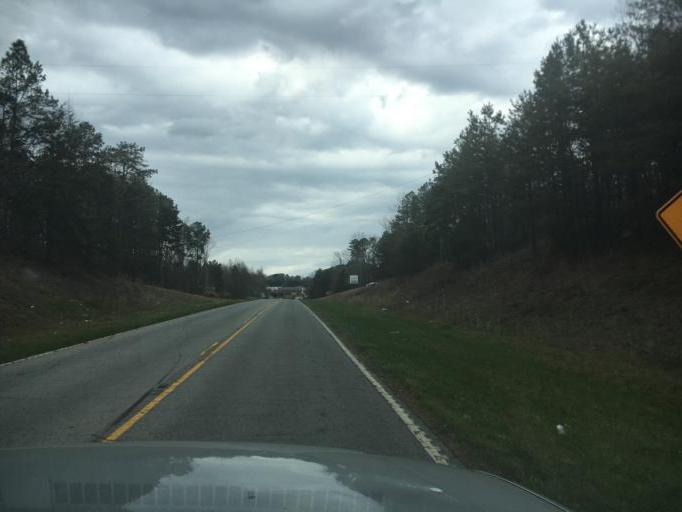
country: US
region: South Carolina
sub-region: Oconee County
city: Walhalla
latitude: 34.7480
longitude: -83.0486
